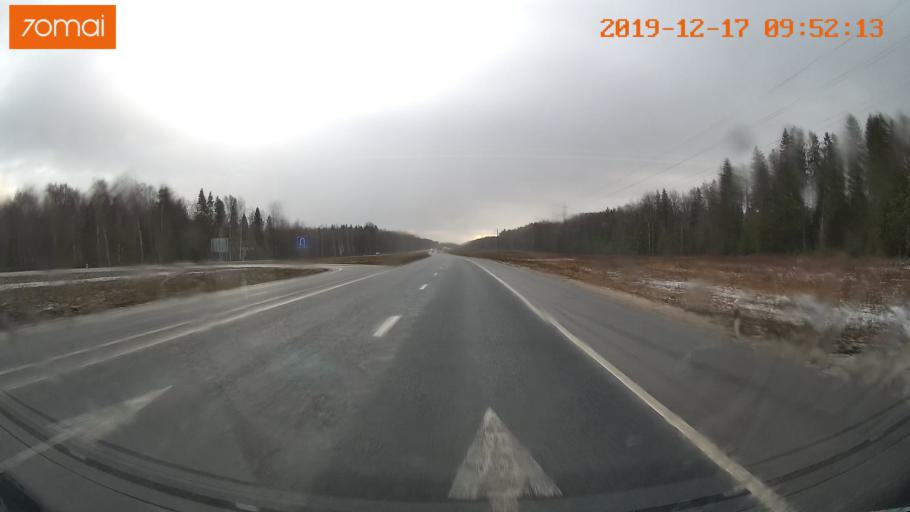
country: RU
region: Vladimir
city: Kommunar
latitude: 56.0352
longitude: 40.5344
